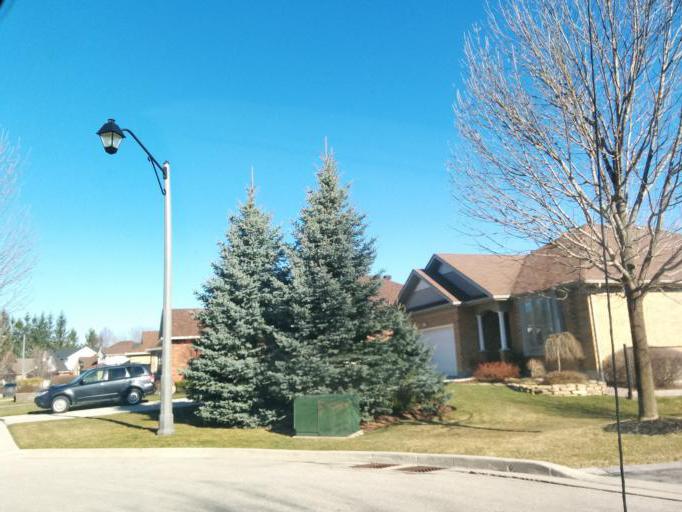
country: CA
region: Ontario
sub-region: Halton
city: Milton
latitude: 43.5187
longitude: -79.8876
